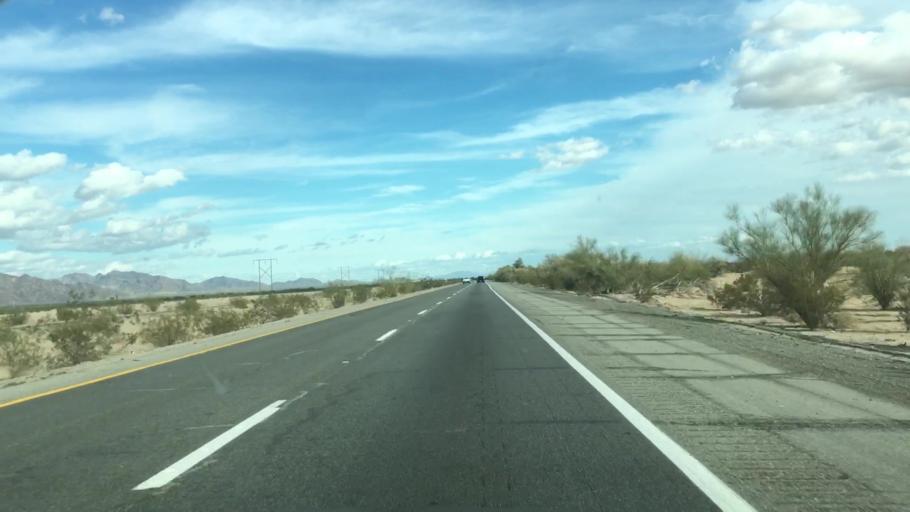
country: US
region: California
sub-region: Riverside County
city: Mesa Verde
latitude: 33.6058
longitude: -114.9454
